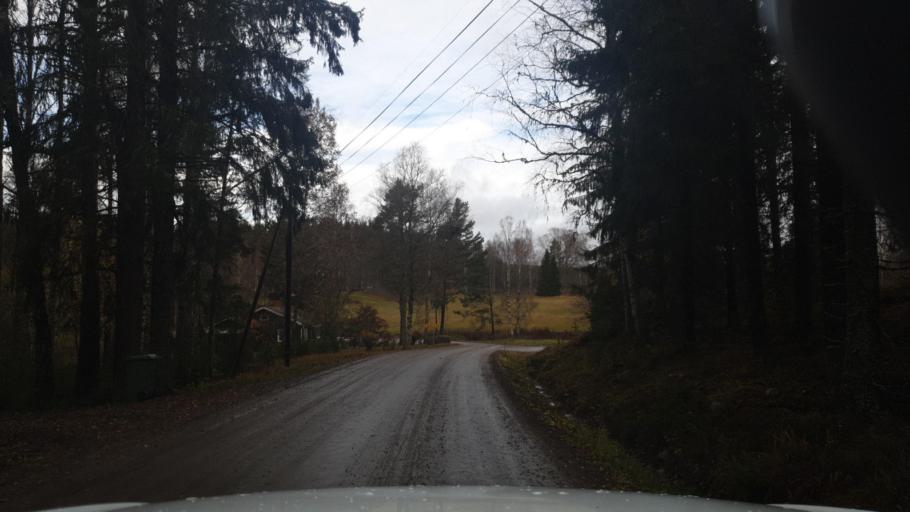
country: NO
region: Ostfold
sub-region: Romskog
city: Romskog
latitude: 59.8266
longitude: 11.9963
